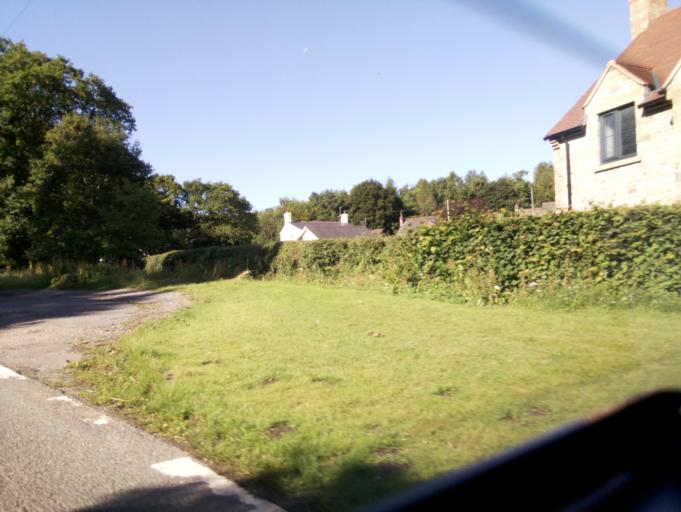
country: GB
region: England
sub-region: Gloucestershire
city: Coleford
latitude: 51.8145
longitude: -2.6232
